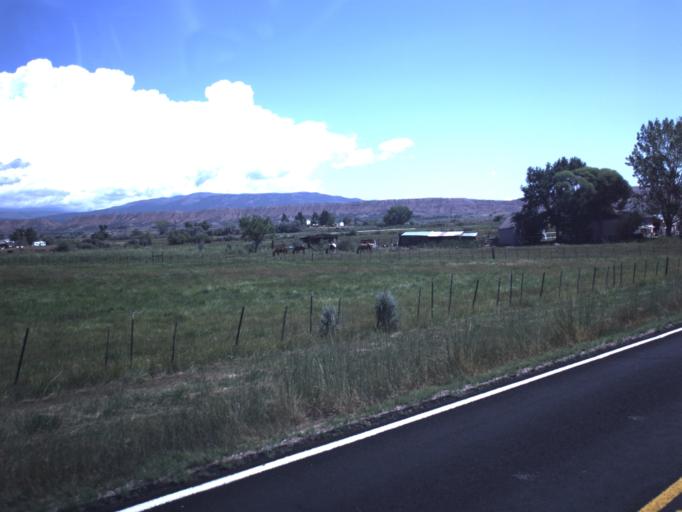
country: US
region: Utah
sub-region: Duchesne County
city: Roosevelt
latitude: 40.4037
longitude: -109.8593
